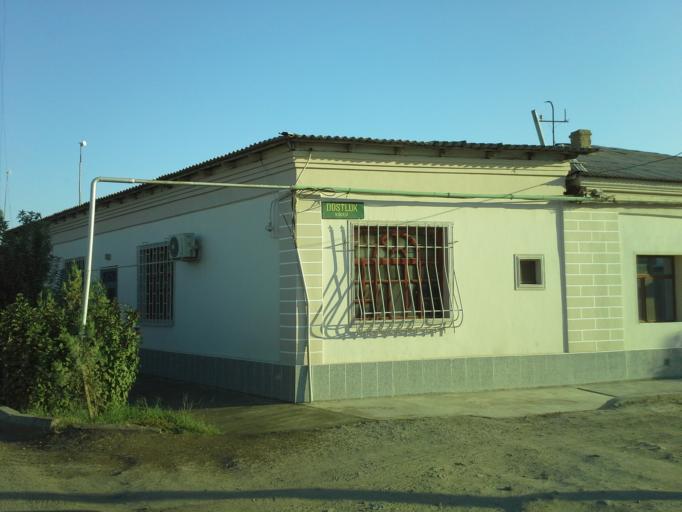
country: TM
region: Dasoguz
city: Dasoguz
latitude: 41.8214
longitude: 59.9794
